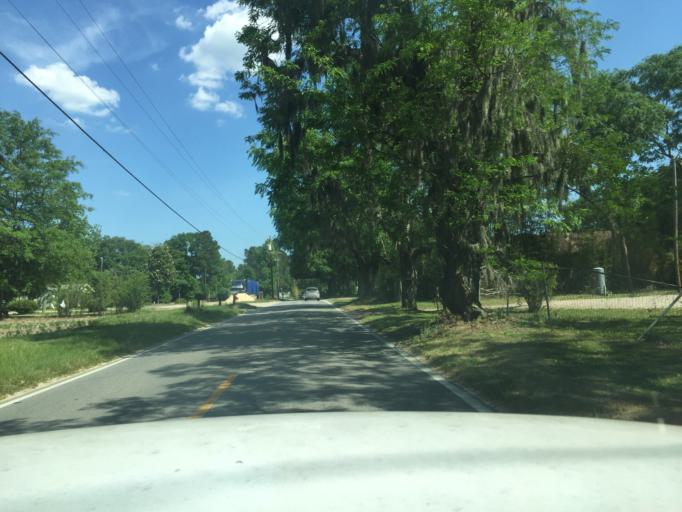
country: US
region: Georgia
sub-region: Chatham County
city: Georgetown
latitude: 31.9995
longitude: -81.2752
